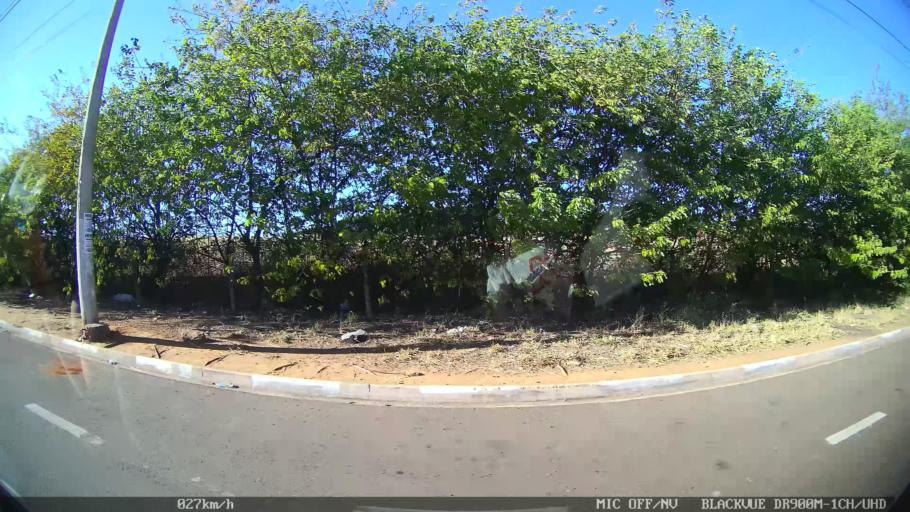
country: BR
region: Sao Paulo
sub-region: Franca
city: Franca
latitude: -20.5732
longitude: -47.3715
